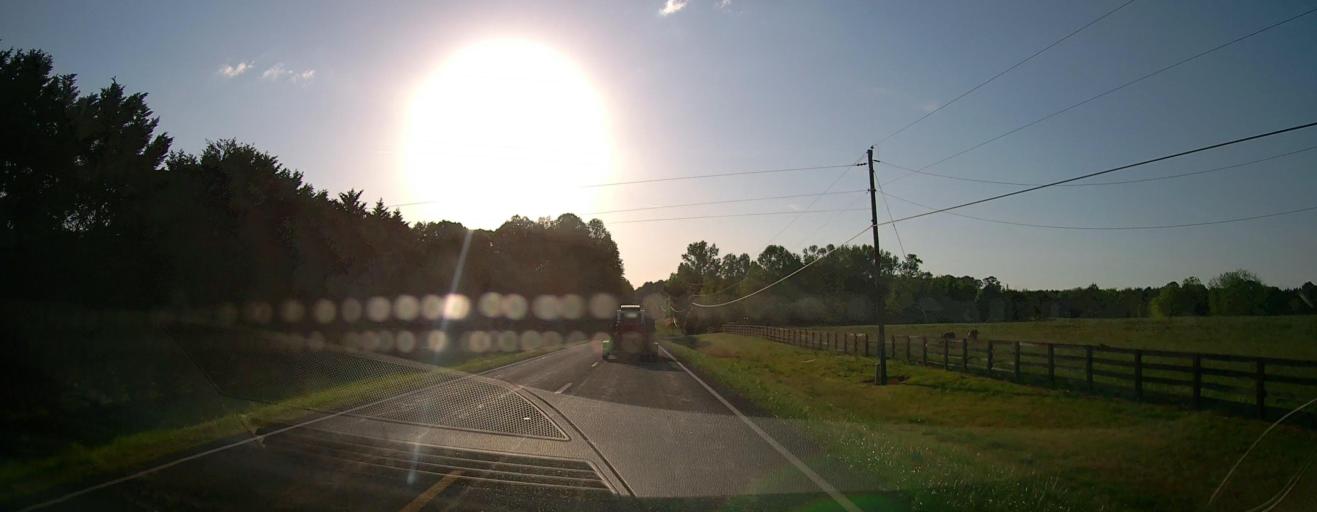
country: US
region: Georgia
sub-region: Walton County
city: Social Circle
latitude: 33.5061
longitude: -83.6607
